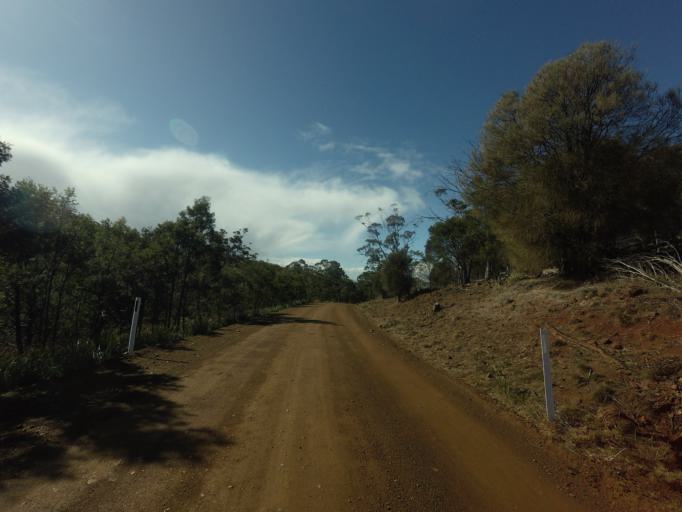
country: AU
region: Tasmania
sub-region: Sorell
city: Sorell
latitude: -42.4061
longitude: 147.9553
